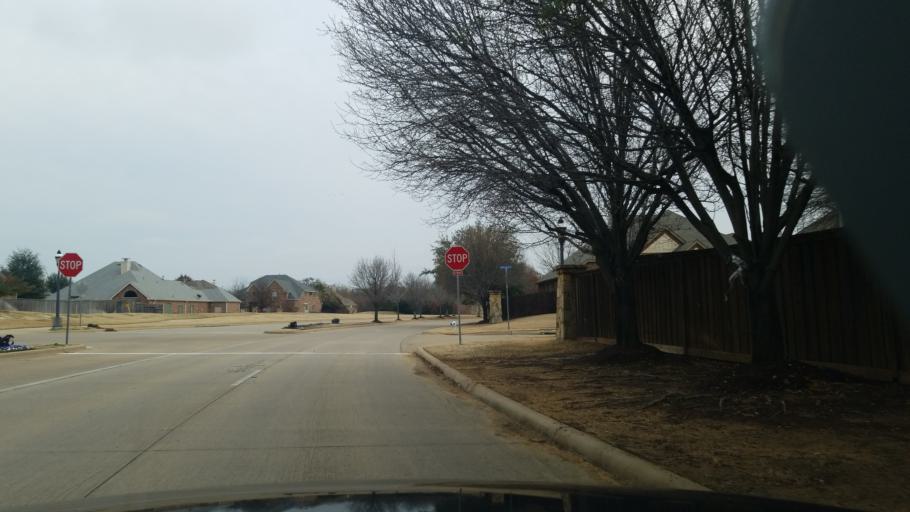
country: US
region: Texas
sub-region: Denton County
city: Shady Shores
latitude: 33.1525
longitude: -97.0431
